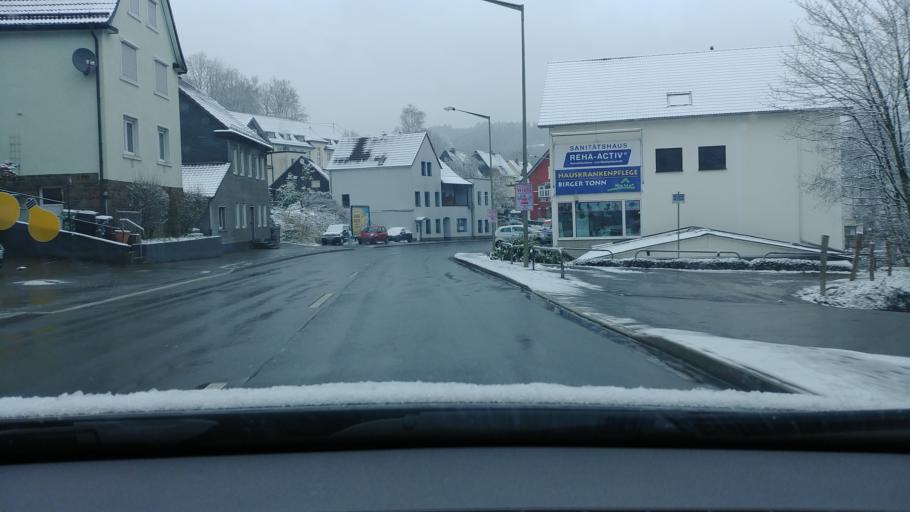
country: DE
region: North Rhine-Westphalia
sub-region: Regierungsbezirk Koln
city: Gummersbach
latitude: 51.0029
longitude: 7.5686
